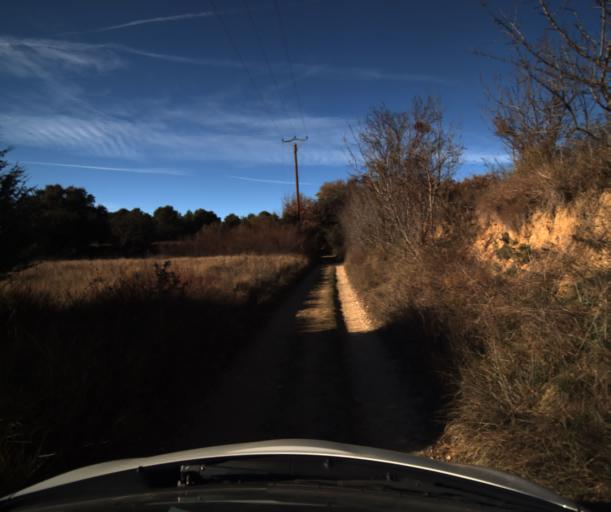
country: FR
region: Provence-Alpes-Cote d'Azur
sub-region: Departement du Vaucluse
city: Pertuis
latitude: 43.7017
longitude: 5.4720
